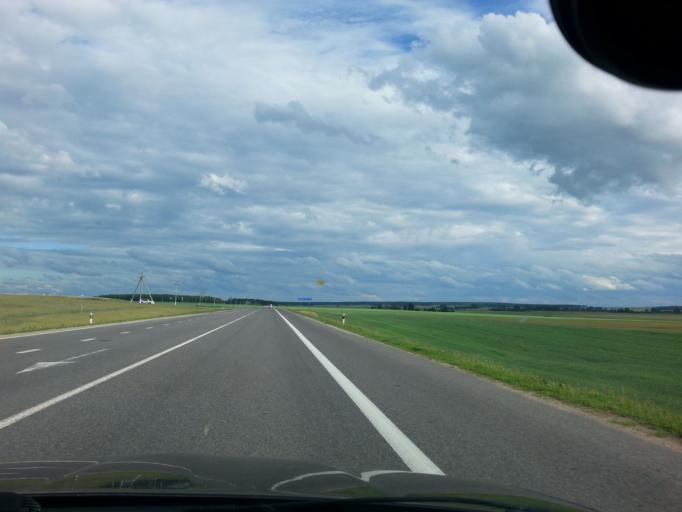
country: BY
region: Grodnenskaya
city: Astravyets
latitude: 54.7553
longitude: 26.0748
